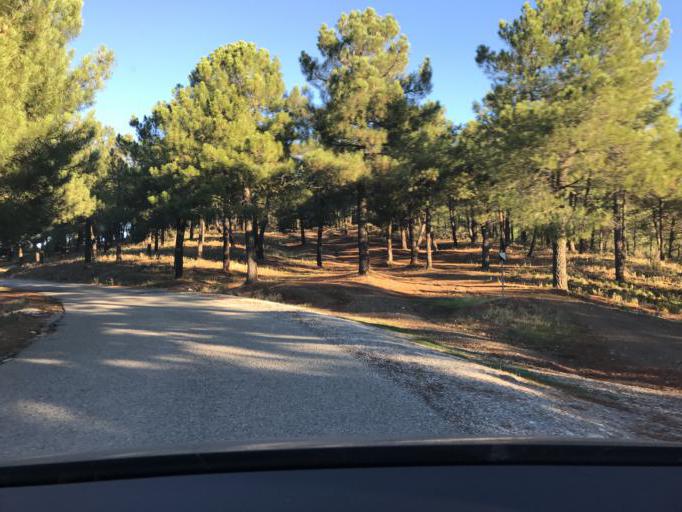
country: ES
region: Andalusia
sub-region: Provincia de Granada
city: Viznar
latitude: 37.2305
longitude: -3.5372
